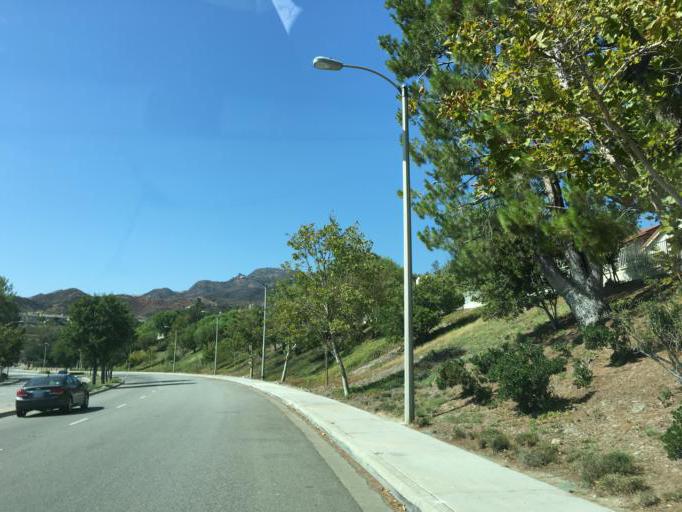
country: US
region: California
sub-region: Los Angeles County
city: Santa Clarita
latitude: 34.3816
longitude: -118.5844
